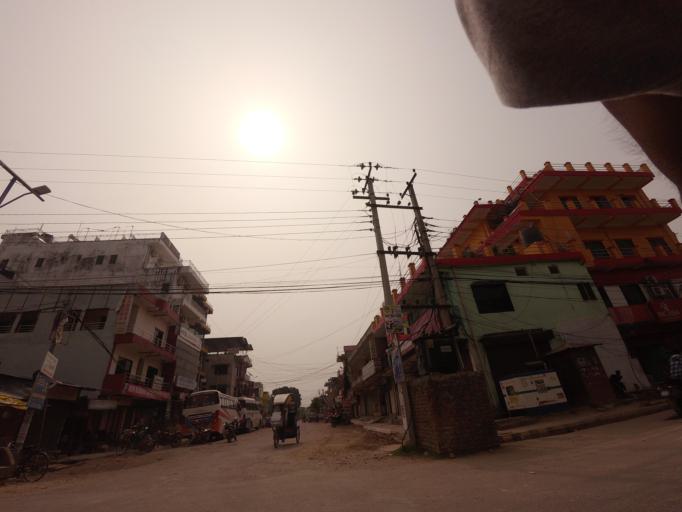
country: IN
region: Uttar Pradesh
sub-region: Maharajganj
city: Nautanwa
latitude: 27.4704
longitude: 83.2839
